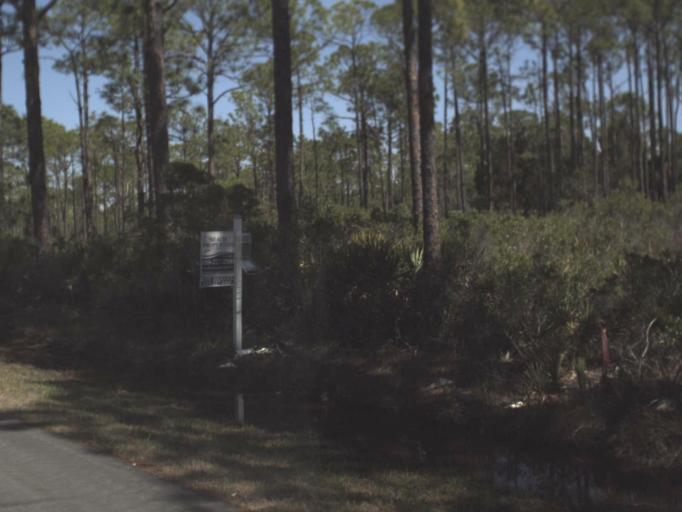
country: US
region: Florida
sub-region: Gulf County
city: Port Saint Joe
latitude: 29.7129
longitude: -85.3030
